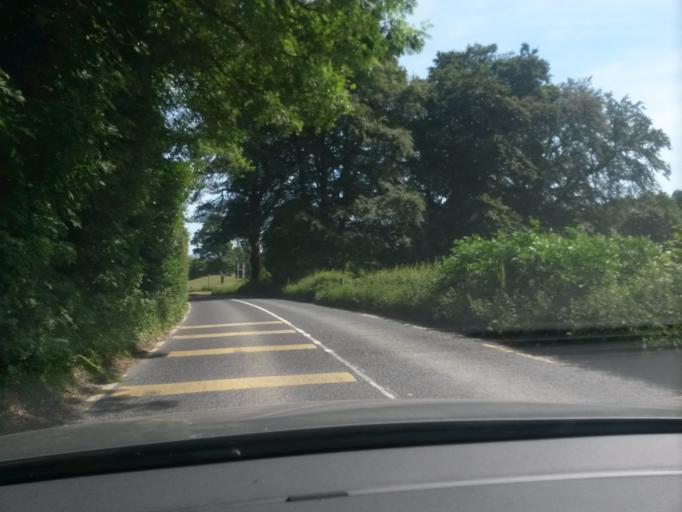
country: IE
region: Leinster
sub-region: Kildare
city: Eadestown
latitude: 53.1780
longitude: -6.5615
